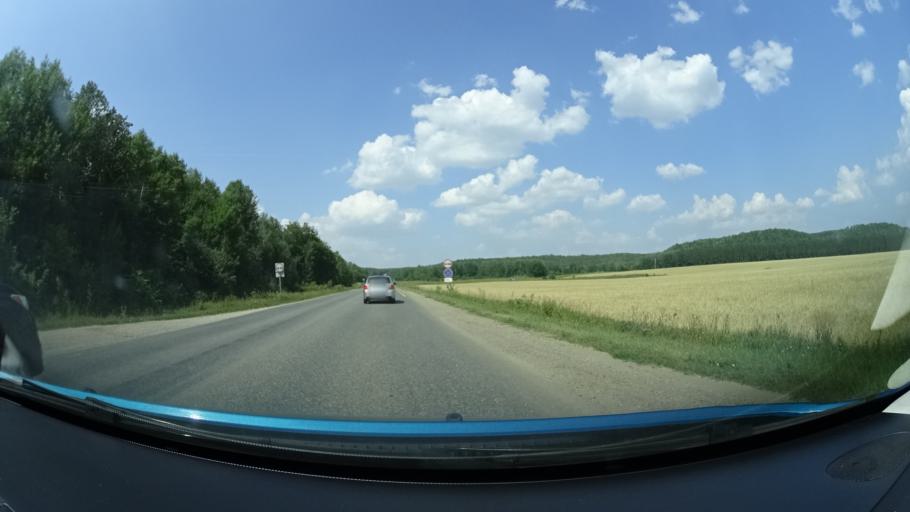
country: RU
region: Bashkortostan
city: Oktyabr'skiy
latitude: 54.4515
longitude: 53.5946
